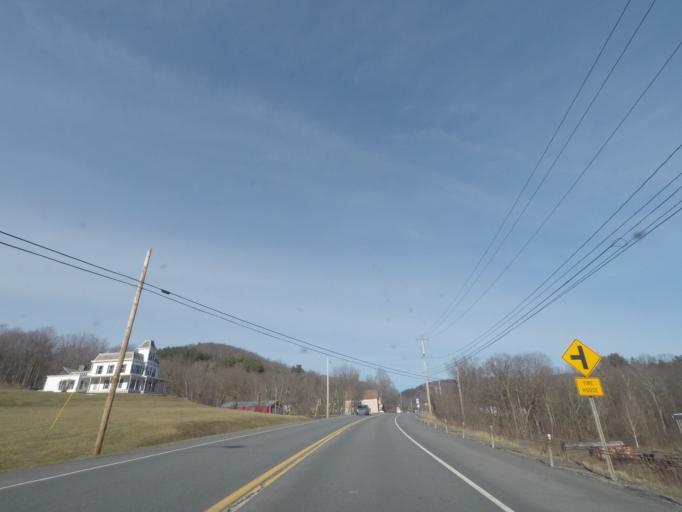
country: US
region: Massachusetts
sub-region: Berkshire County
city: Williamstown
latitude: 42.7487
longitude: -73.3484
